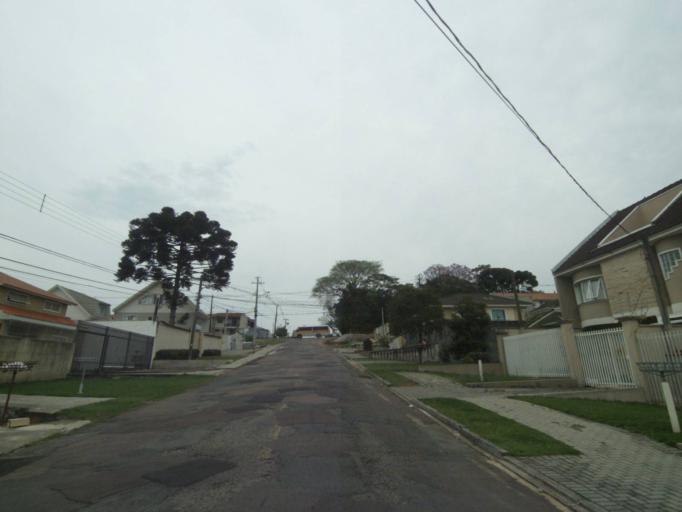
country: BR
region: Parana
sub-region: Pinhais
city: Pinhais
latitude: -25.4167
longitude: -49.2048
